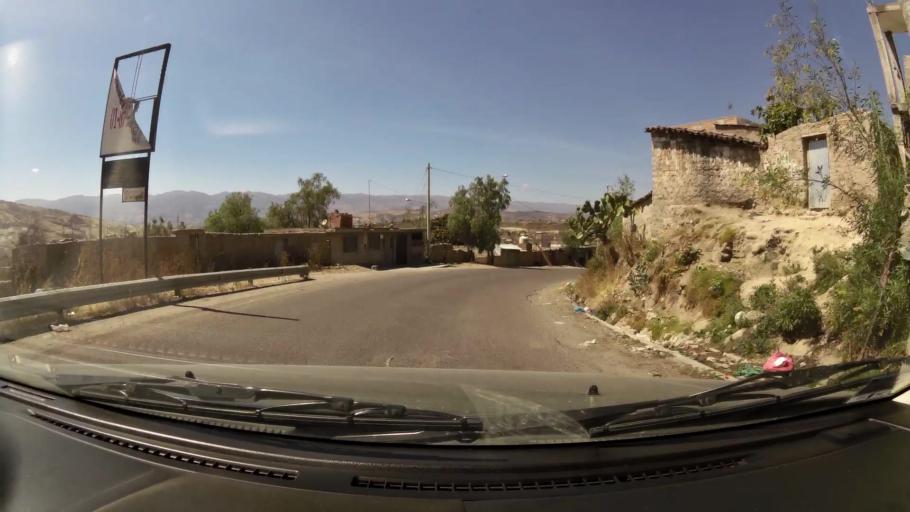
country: PE
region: Ayacucho
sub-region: Provincia de Huamanga
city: Ayacucho
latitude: -13.1447
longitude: -74.2132
